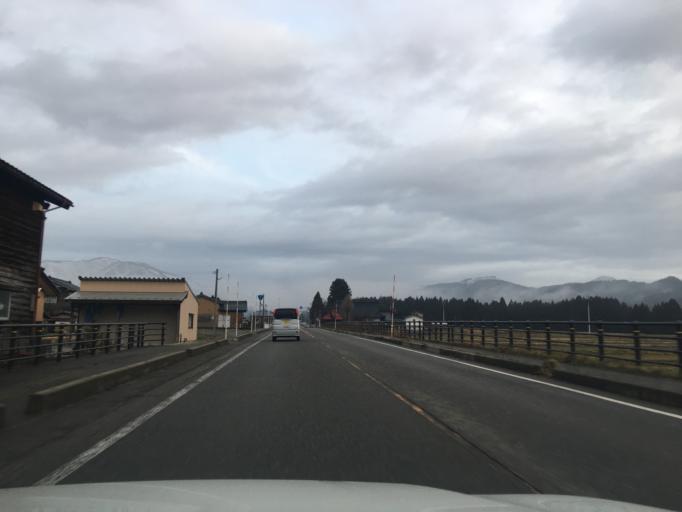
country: JP
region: Niigata
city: Murakami
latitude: 38.3276
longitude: 139.5555
